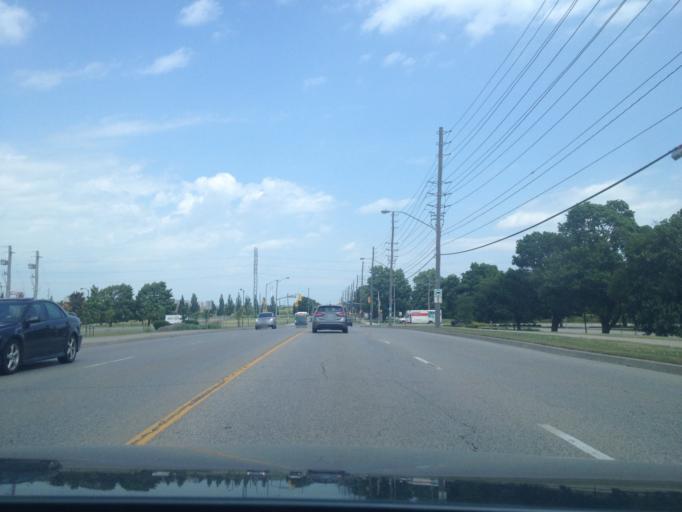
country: CA
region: Ontario
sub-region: Wellington County
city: Guelph
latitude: 43.5554
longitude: -80.2907
